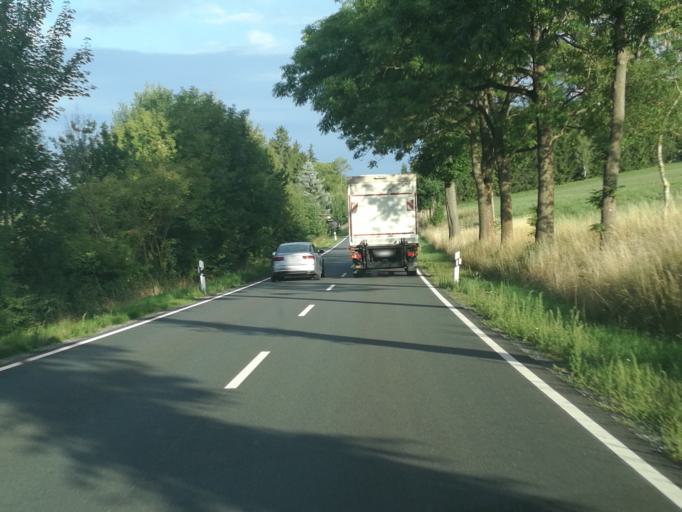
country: DE
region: Saxony
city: Eichigt
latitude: 50.3370
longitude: 12.2077
